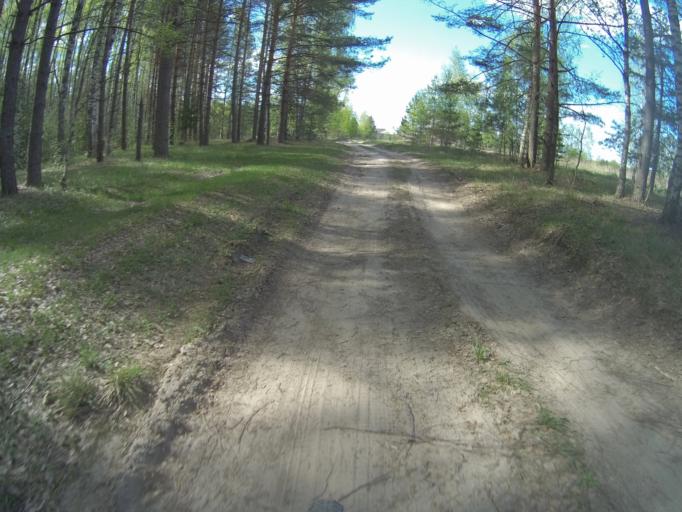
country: RU
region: Vladimir
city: Vorsha
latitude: 55.9656
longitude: 40.1852
